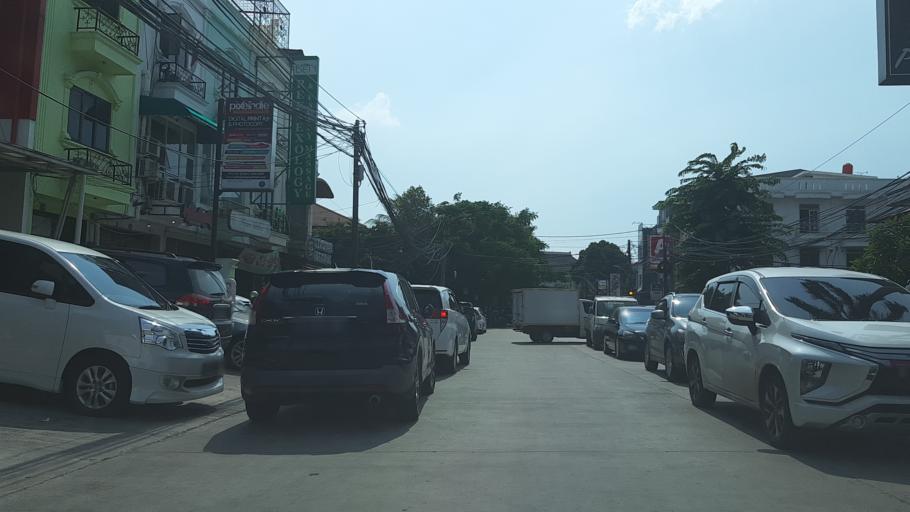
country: ID
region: Jakarta Raya
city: Jakarta
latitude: -6.1698
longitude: 106.7670
